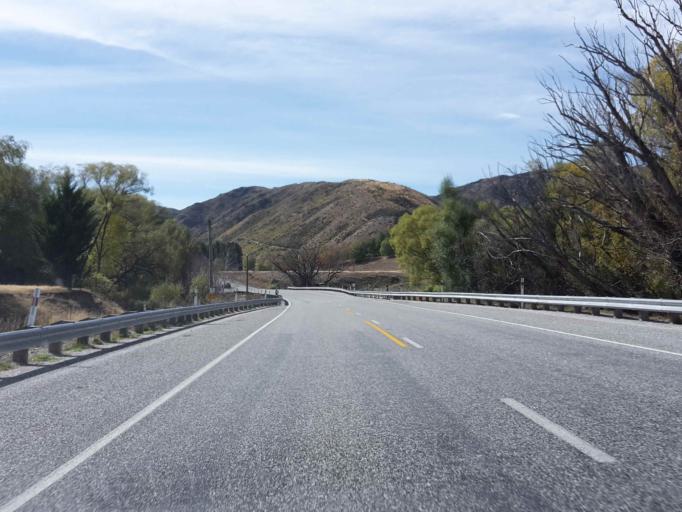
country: NZ
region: Otago
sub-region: Queenstown-Lakes District
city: Wanaka
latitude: -44.6411
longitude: 169.5056
